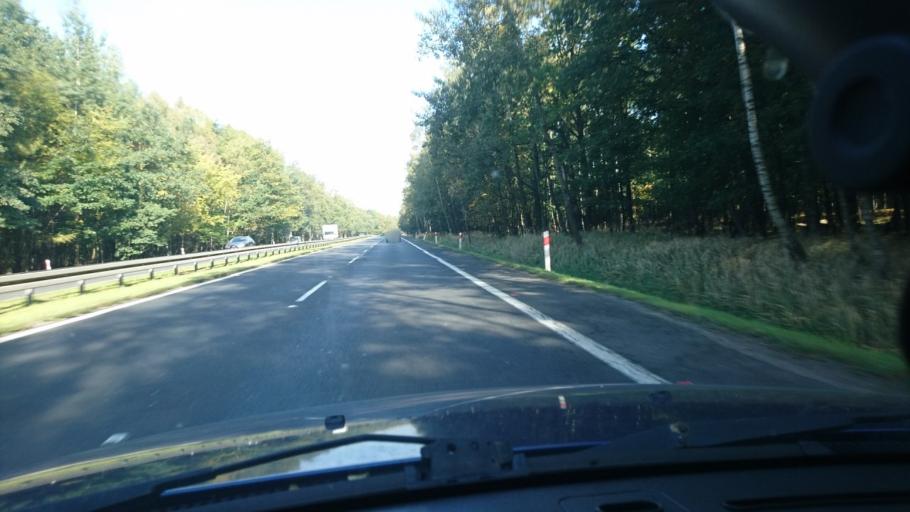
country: PL
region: Silesian Voivodeship
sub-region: Tychy
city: Cielmice
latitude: 50.1415
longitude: 19.0245
